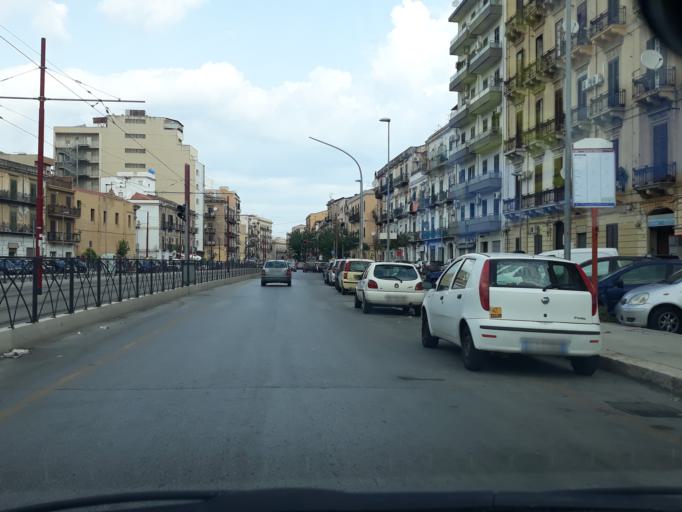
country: IT
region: Sicily
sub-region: Palermo
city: Palermo
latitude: 38.1092
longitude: 13.3704
